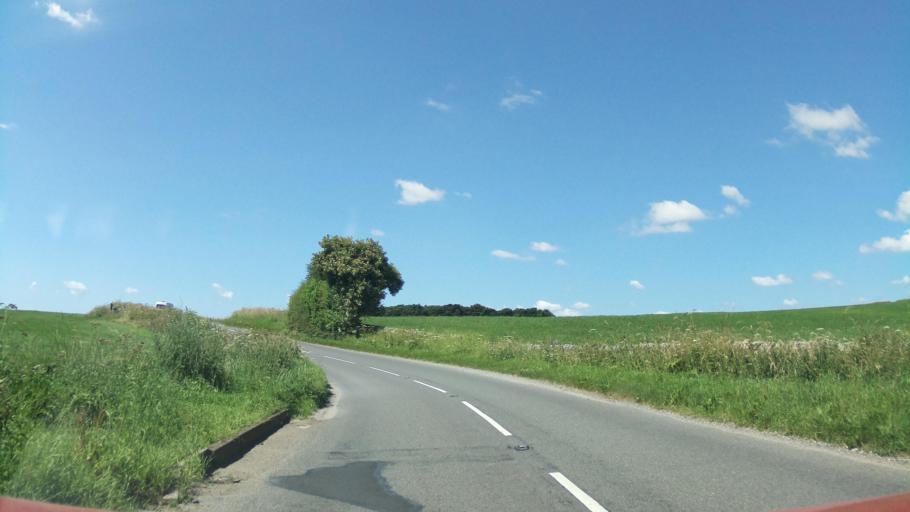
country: GB
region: England
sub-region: Derbyshire
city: Bakewell
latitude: 53.1985
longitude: -1.7332
